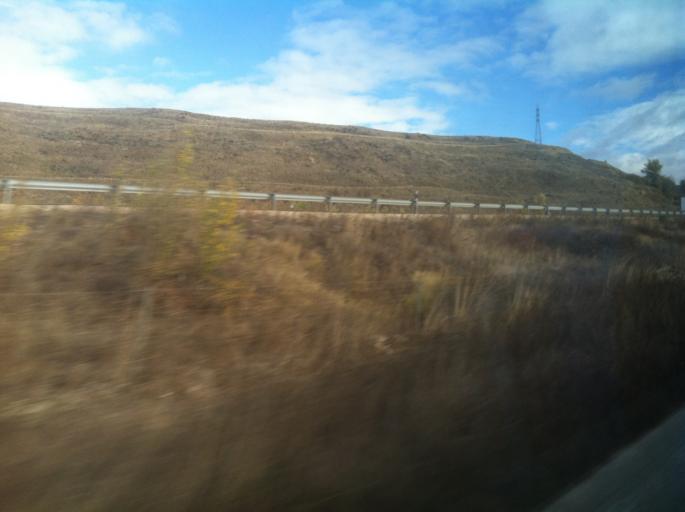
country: ES
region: Castille and Leon
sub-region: Provincia de Burgos
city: Castil de Peones
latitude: 42.4888
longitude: -3.3821
